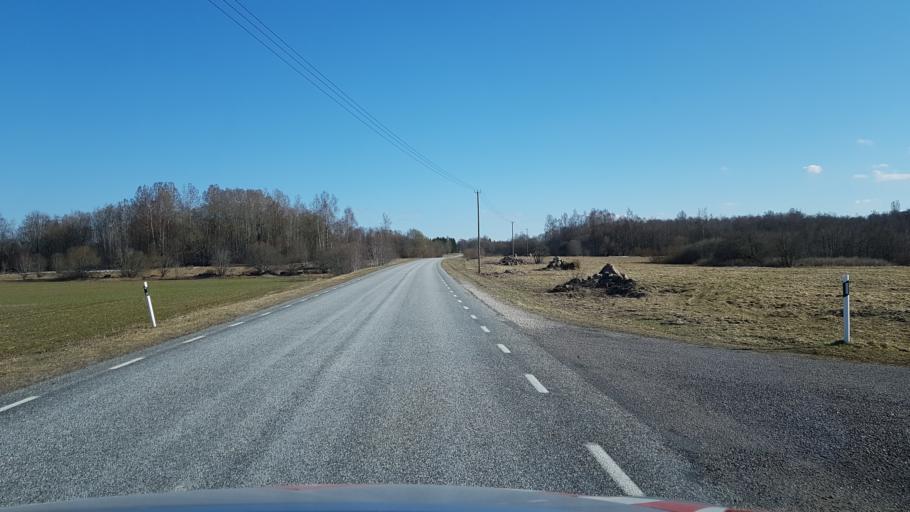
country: EE
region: Laeaene-Virumaa
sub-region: Haljala vald
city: Haljala
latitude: 59.4857
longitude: 26.1510
